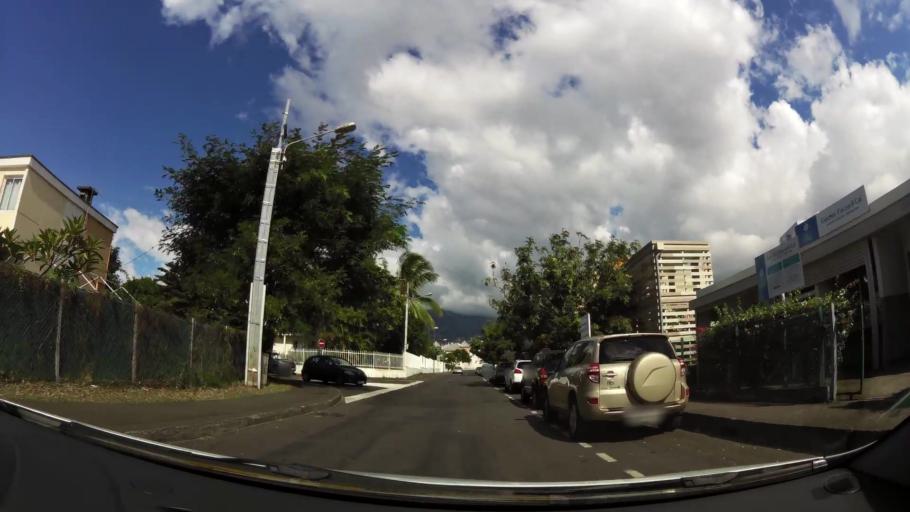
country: RE
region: Reunion
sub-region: Reunion
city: Saint-Denis
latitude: -20.8935
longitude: 55.4890
